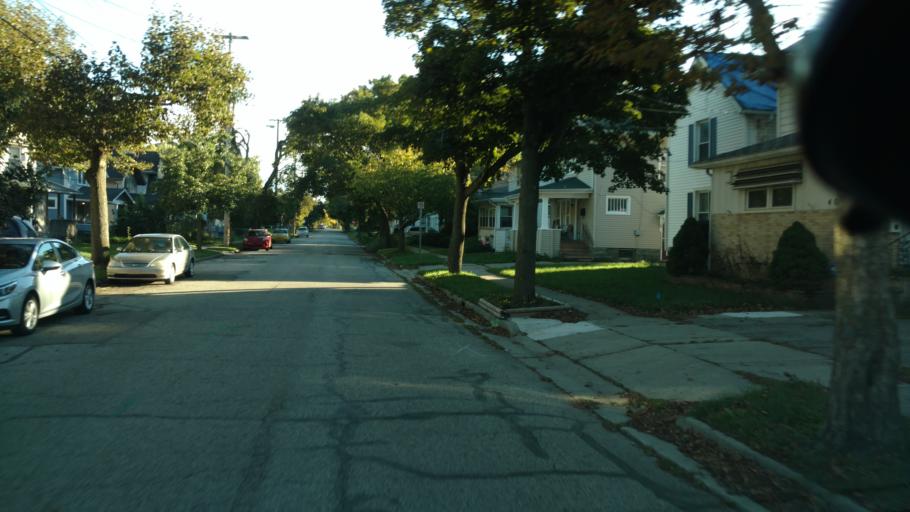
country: US
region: Michigan
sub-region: Ingham County
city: Lansing
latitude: 42.7374
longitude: -84.5212
